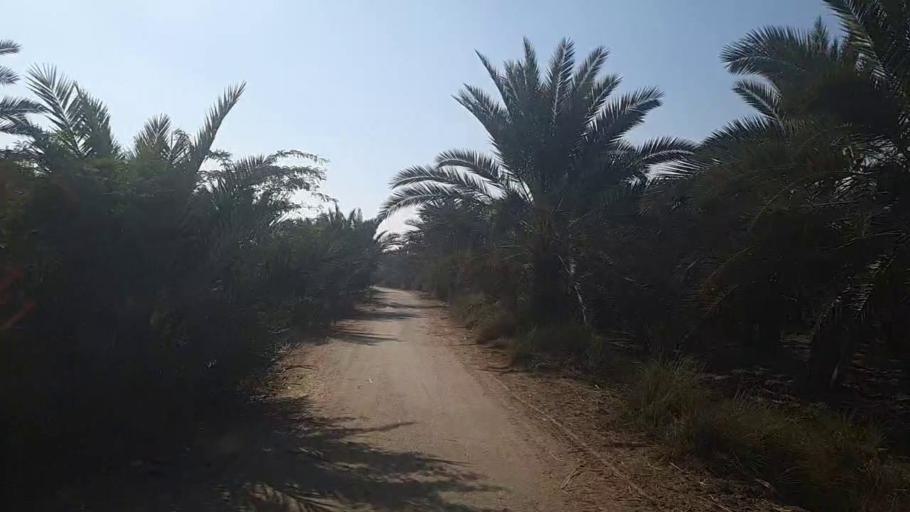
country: PK
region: Sindh
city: Khairpur
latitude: 27.4425
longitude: 68.7364
